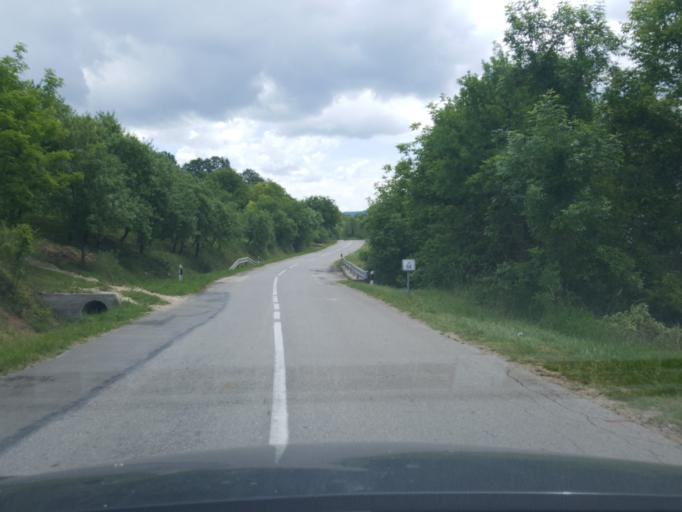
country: RS
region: Central Serbia
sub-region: Zajecarski Okrug
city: Soko Banja
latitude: 43.6471
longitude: 21.9282
